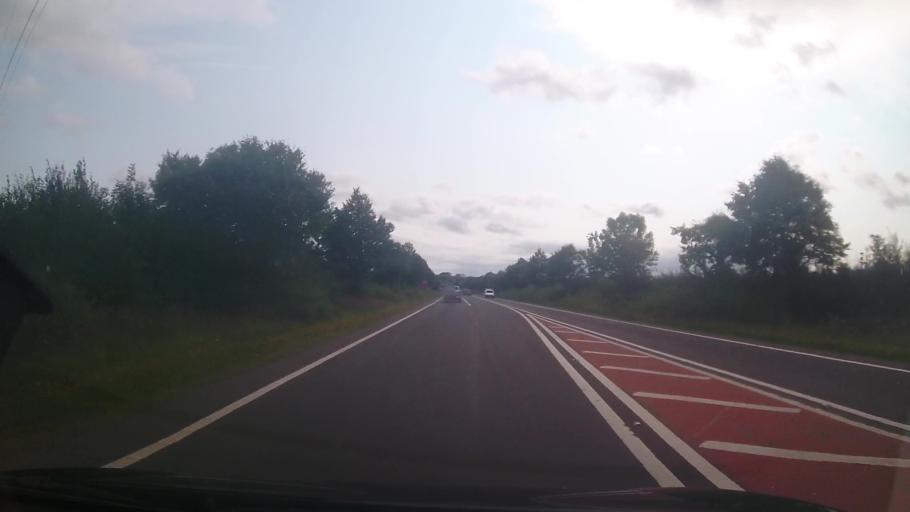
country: GB
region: England
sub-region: Shropshire
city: Shrewsbury
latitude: 52.7112
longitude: -2.7027
